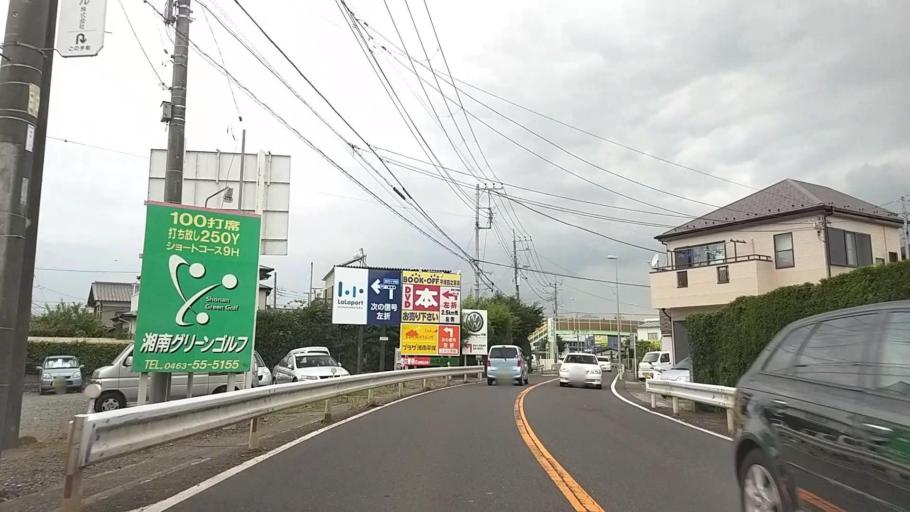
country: JP
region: Kanagawa
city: Hiratsuka
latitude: 35.3749
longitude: 139.3641
